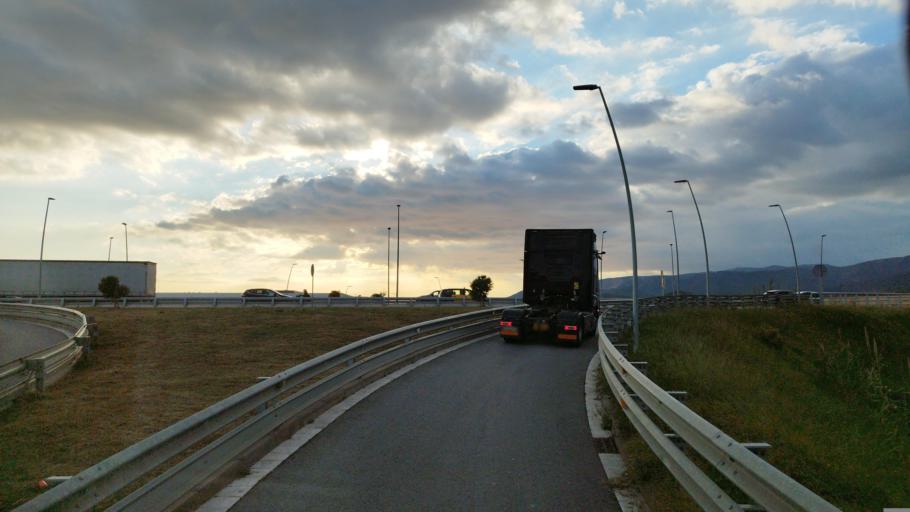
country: ES
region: Catalonia
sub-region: Provincia de Barcelona
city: Viladecans
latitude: 41.3064
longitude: 2.0220
